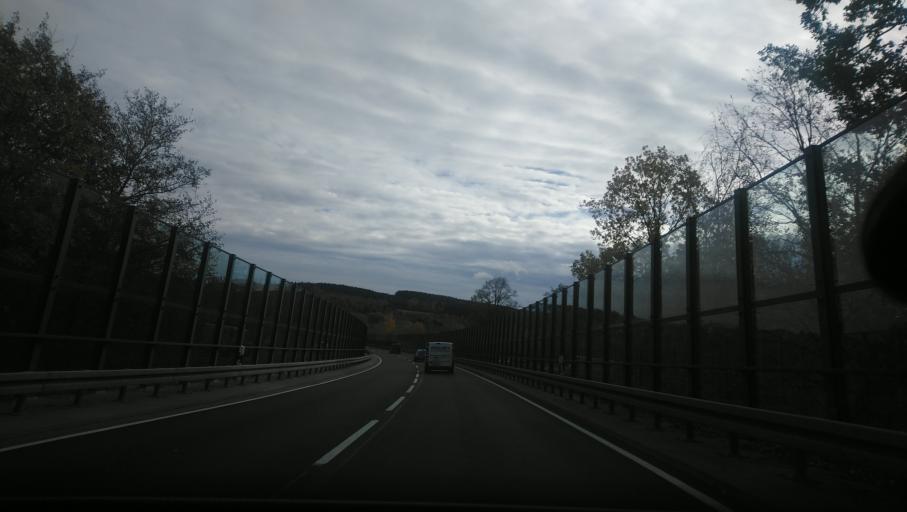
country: DE
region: Saxony
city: Stollberg
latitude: 50.6979
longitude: 12.7712
